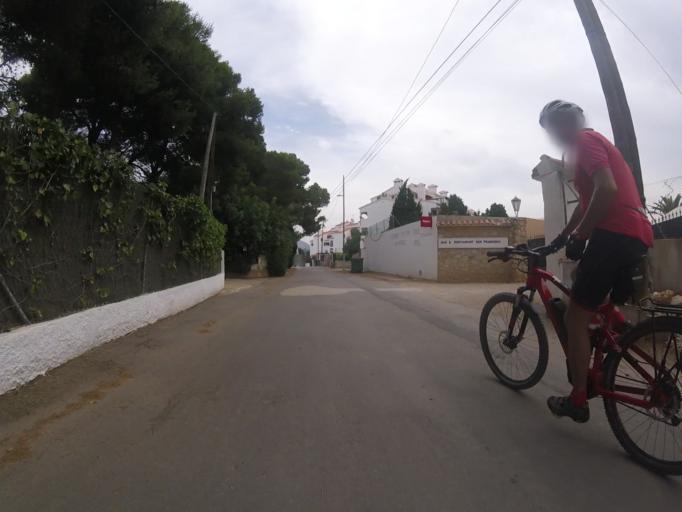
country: ES
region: Valencia
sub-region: Provincia de Castello
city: Alcoceber
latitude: 40.2363
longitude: 0.2707
